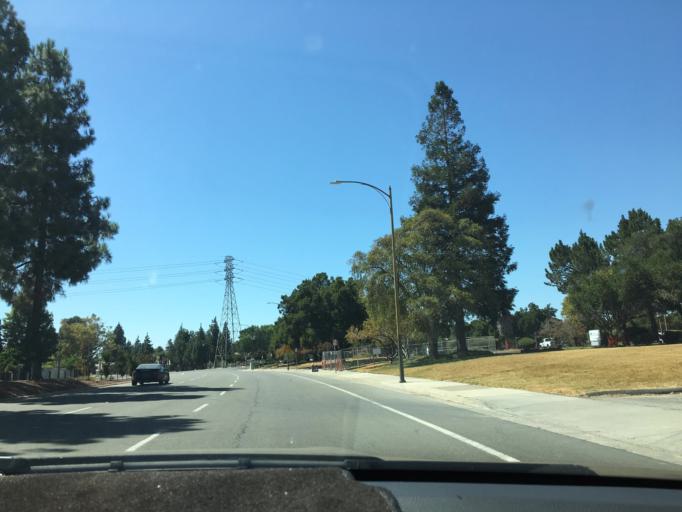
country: US
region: California
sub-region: Santa Clara County
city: Seven Trees
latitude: 37.2360
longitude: -121.7921
